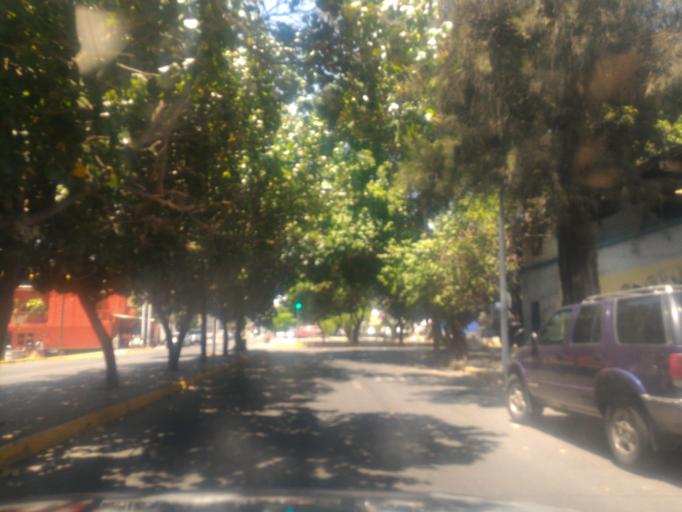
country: MX
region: Jalisco
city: Tlaquepaque
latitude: 20.6766
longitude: -103.3008
